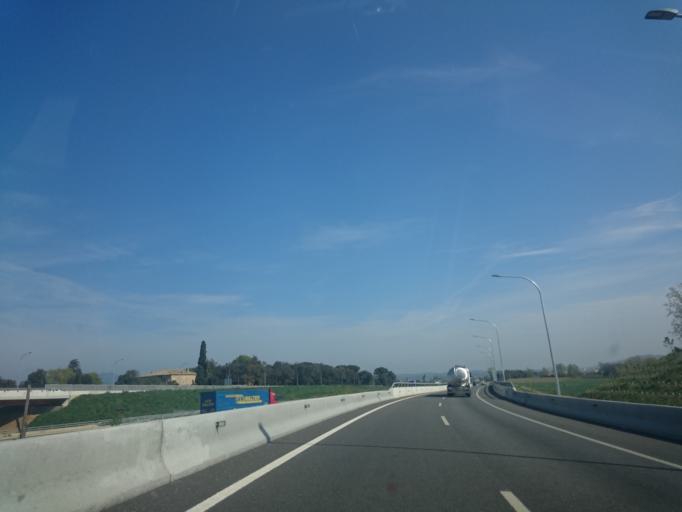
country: ES
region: Catalonia
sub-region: Provincia de Girona
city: Fornells de la Selva
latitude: 41.9334
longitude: 2.7873
